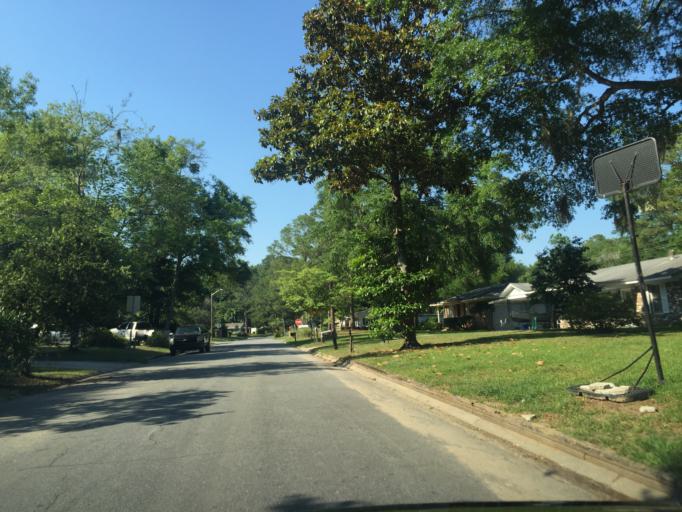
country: US
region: Georgia
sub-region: Chatham County
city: Montgomery
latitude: 31.9859
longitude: -81.1270
